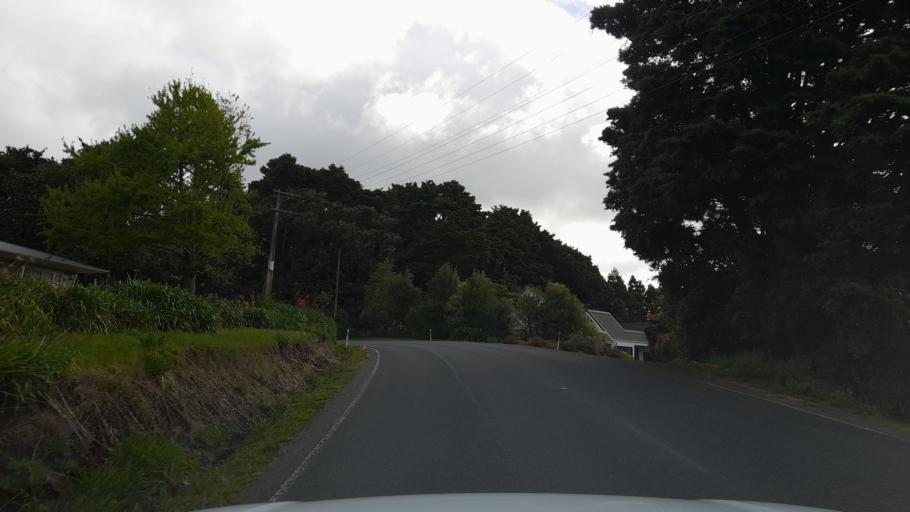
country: NZ
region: Northland
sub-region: Whangarei
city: Maungatapere
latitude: -35.7525
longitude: 174.2473
